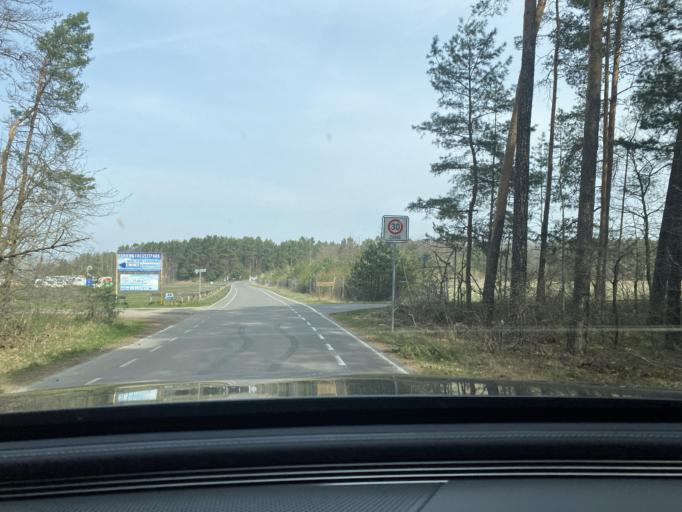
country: DE
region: Brandenburg
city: Welzow
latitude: 51.4947
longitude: 14.1347
